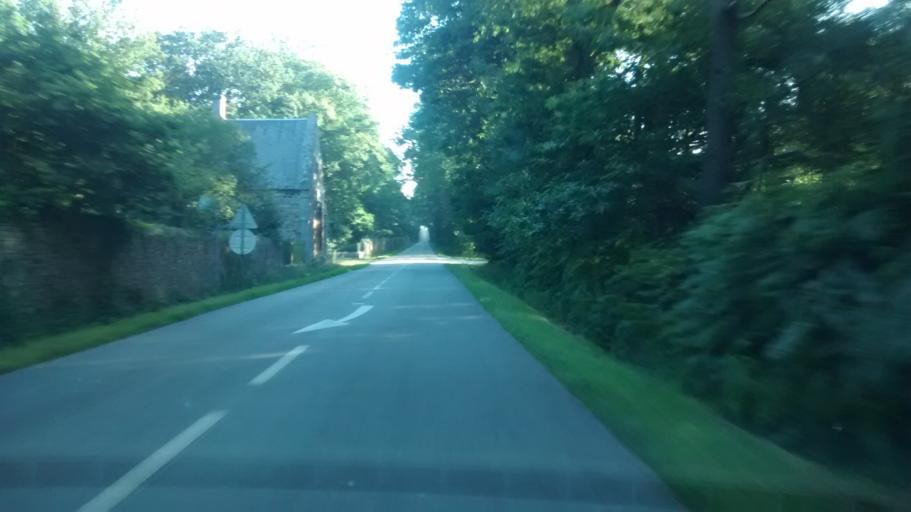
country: FR
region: Brittany
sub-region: Departement du Morbihan
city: Molac
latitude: 47.7560
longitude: -2.4378
